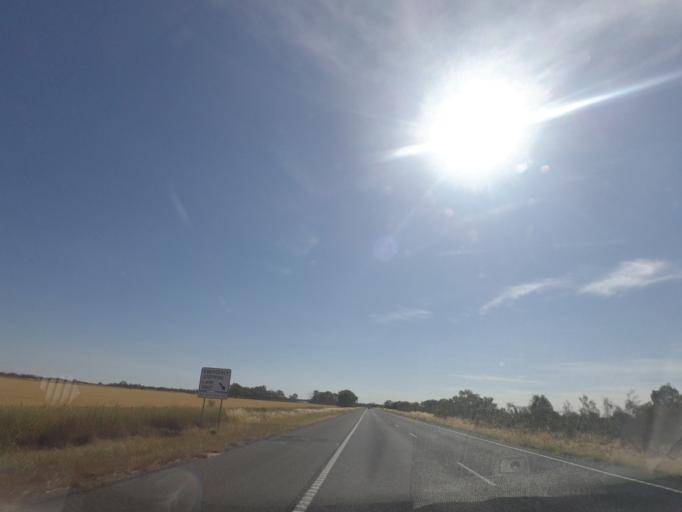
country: AU
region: Victoria
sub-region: Greater Shepparton
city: Shepparton
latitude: -36.6736
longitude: 145.2569
